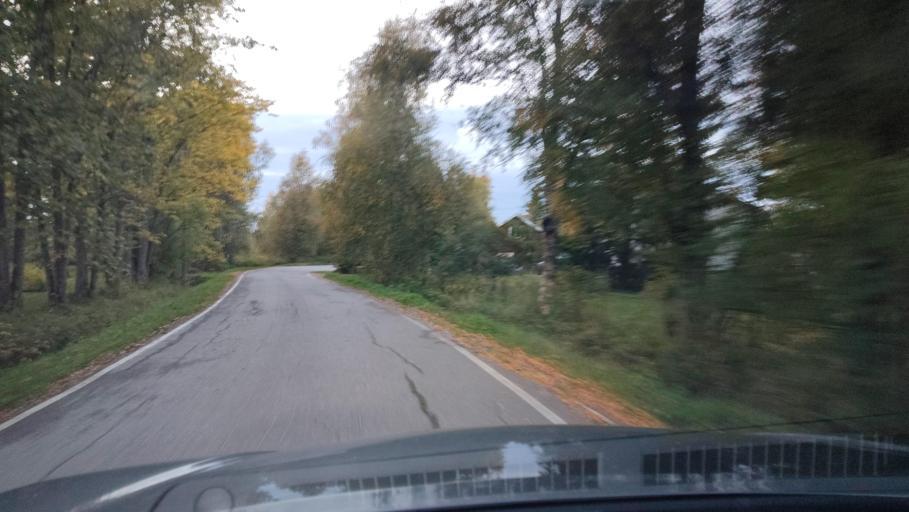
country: FI
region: Ostrobothnia
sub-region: Sydosterbotten
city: Kristinestad
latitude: 62.2574
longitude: 21.5094
